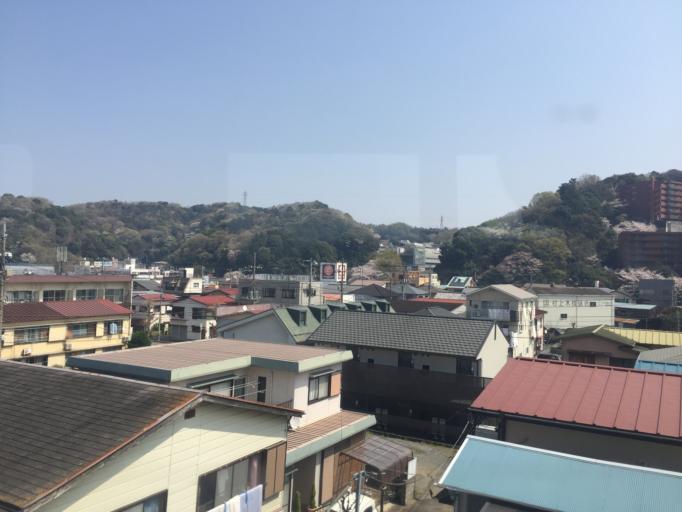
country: JP
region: Shizuoka
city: Ito
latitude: 34.9546
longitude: 139.0869
